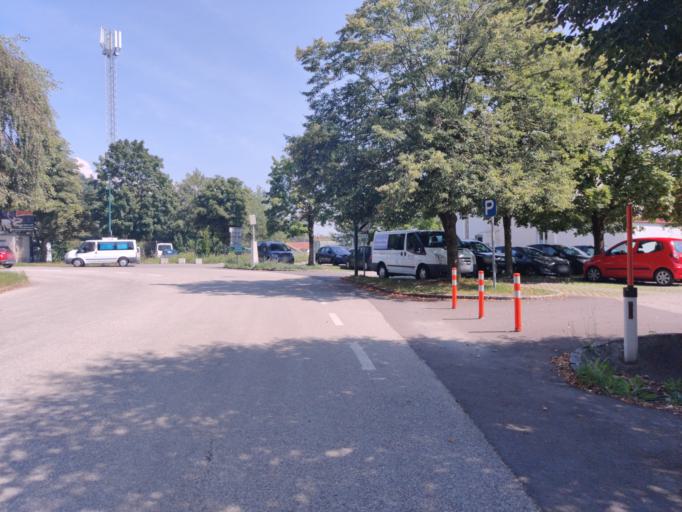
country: AT
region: Upper Austria
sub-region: Politischer Bezirk Linz-Land
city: Leonding
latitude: 48.3118
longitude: 14.2412
